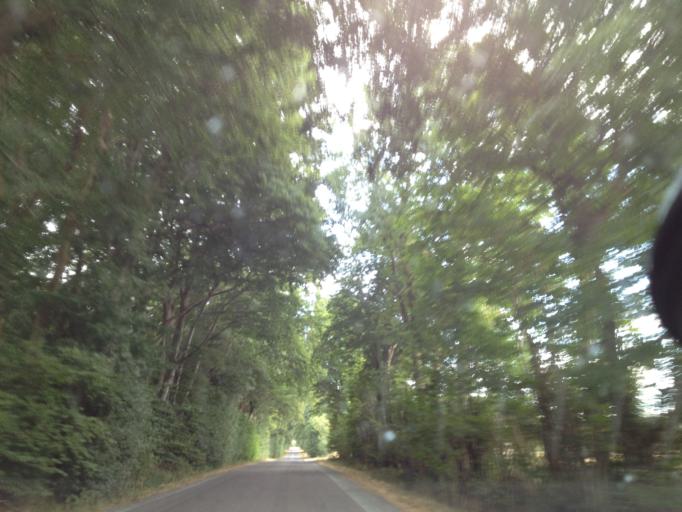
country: DK
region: Zealand
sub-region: Guldborgsund Kommune
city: Sakskobing
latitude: 54.7804
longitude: 11.6528
